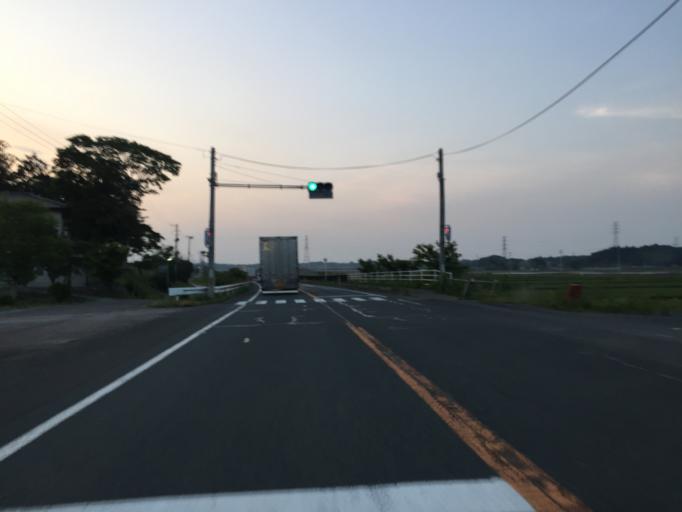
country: JP
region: Fukushima
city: Namie
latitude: 37.5855
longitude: 141.0086
